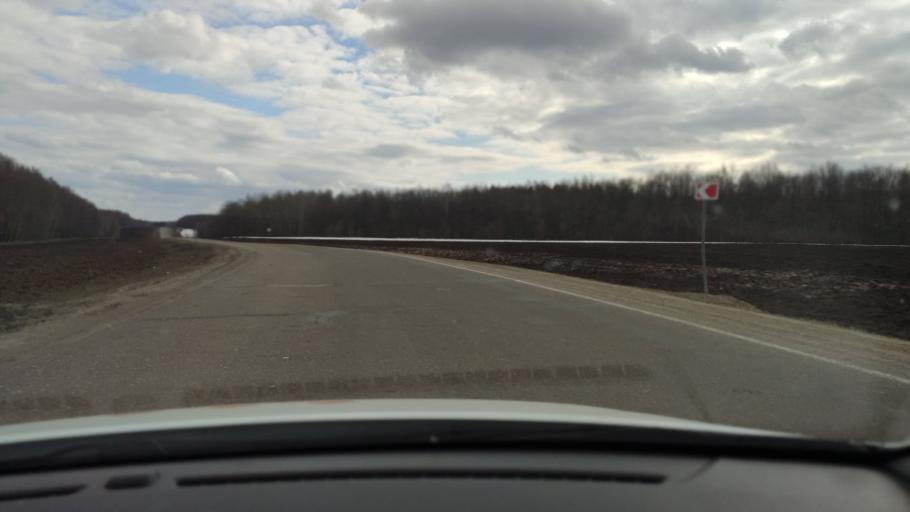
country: RU
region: Tatarstan
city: Vysokaya Gora
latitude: 56.0862
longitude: 49.1827
